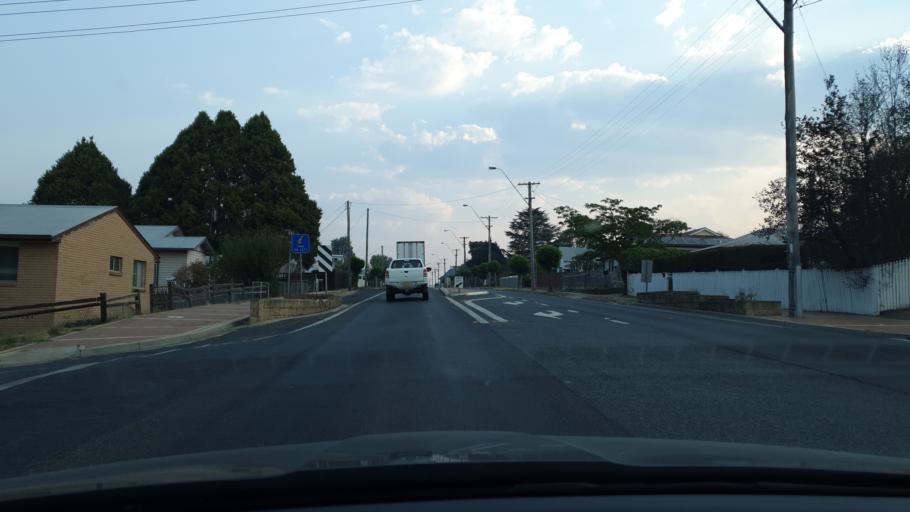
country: AU
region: New South Wales
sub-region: Tenterfield Municipality
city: Carrolls Creek
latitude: -29.0475
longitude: 152.0203
